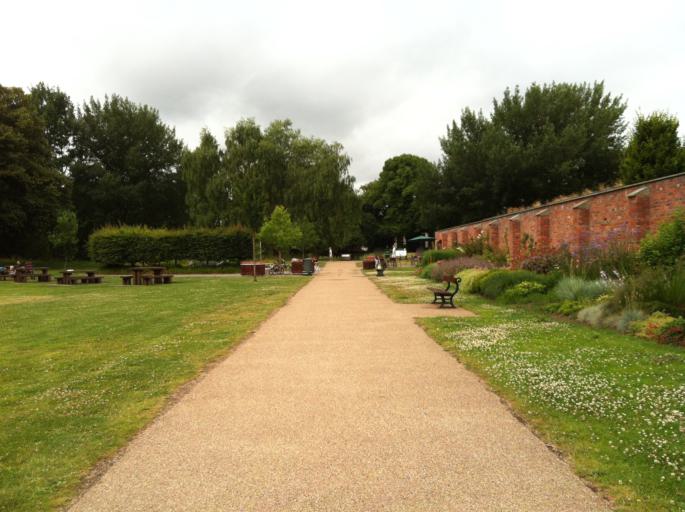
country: GB
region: Wales
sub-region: Cardiff
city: Cardiff
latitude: 51.4874
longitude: -3.1876
